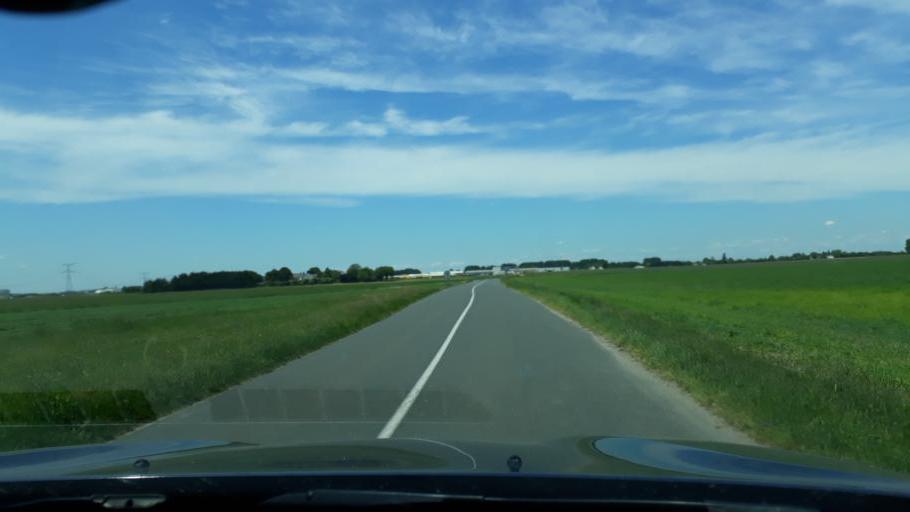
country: FR
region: Centre
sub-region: Departement du Loiret
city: Pithiviers-le-Vieil
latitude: 48.1206
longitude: 2.2099
